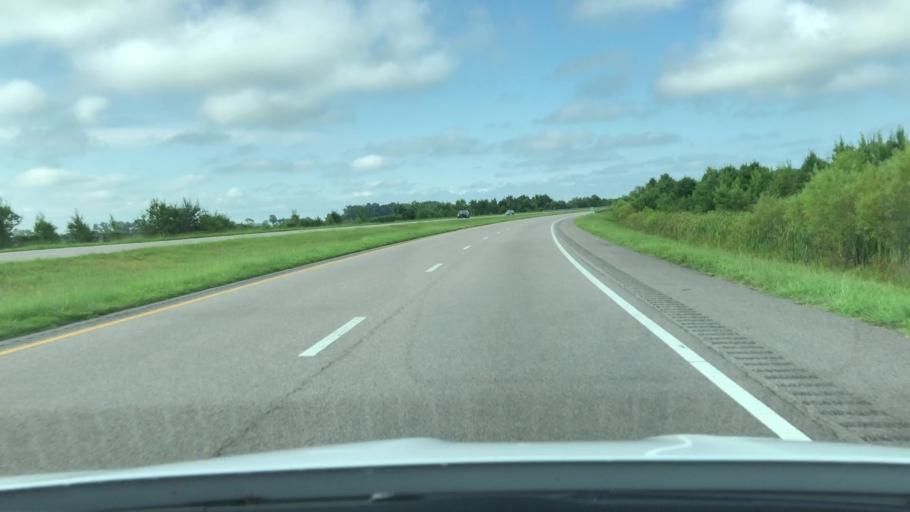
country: US
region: Virginia
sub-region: City of Portsmouth
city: Portsmouth Heights
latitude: 36.6221
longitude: -76.3660
